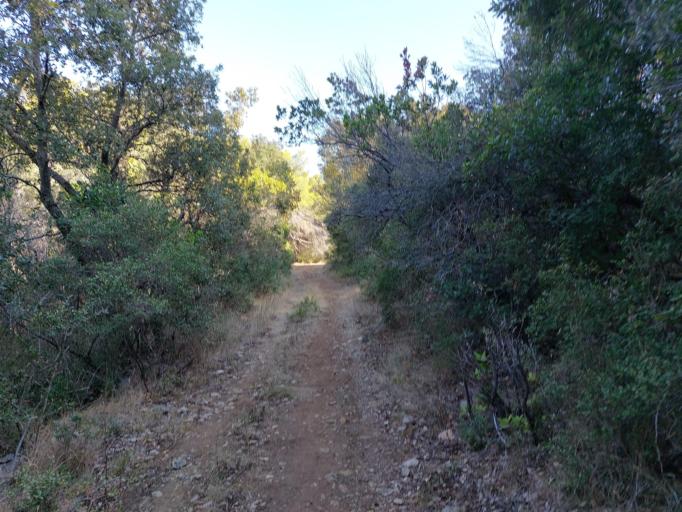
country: HR
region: Dubrovacko-Neretvanska
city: Smokvica
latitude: 42.7556
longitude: 16.8106
